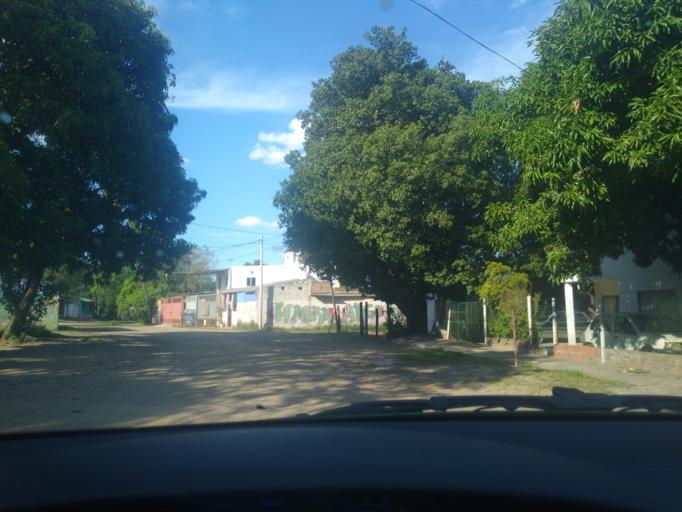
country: AR
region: Chaco
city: Barranqueras
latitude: -27.4785
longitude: -58.9276
